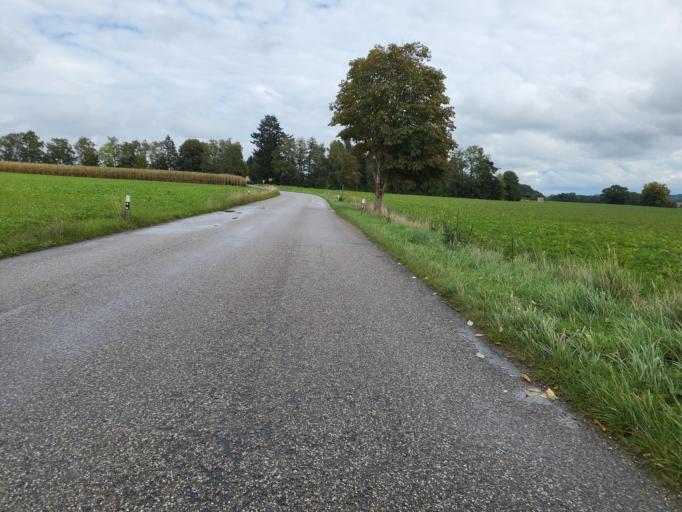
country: DE
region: Bavaria
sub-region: Upper Bavaria
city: Alling
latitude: 48.1561
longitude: 11.2742
